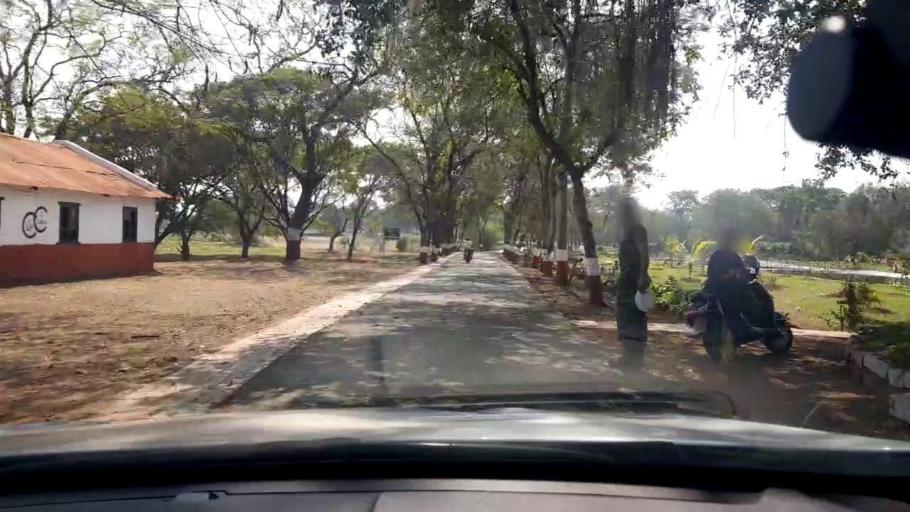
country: IN
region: Maharashtra
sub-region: Pune Division
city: Shivaji Nagar
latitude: 18.5437
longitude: 73.8559
